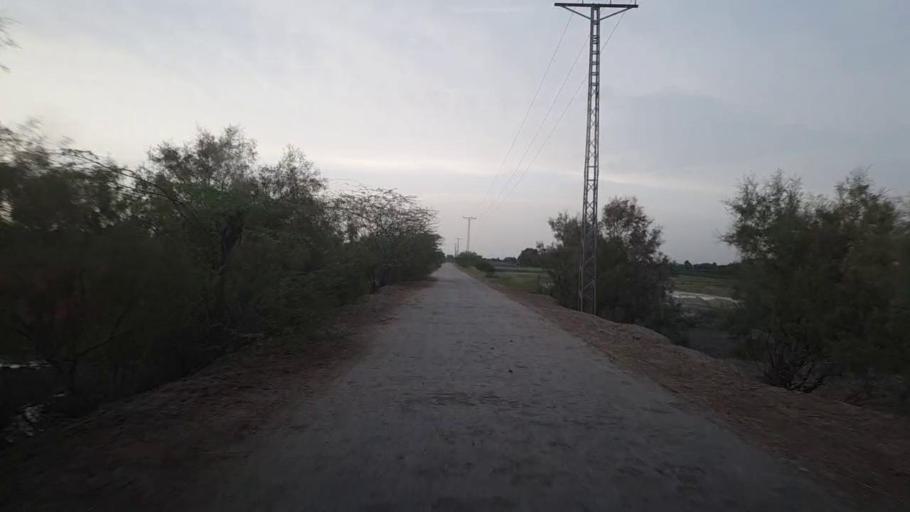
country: PK
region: Sindh
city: Karaundi
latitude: 27.0074
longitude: 68.3539
